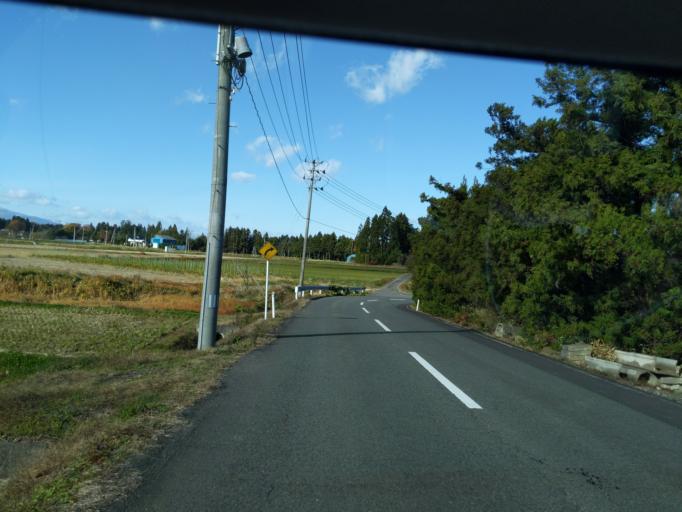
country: JP
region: Iwate
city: Mizusawa
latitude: 39.0676
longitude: 141.1117
